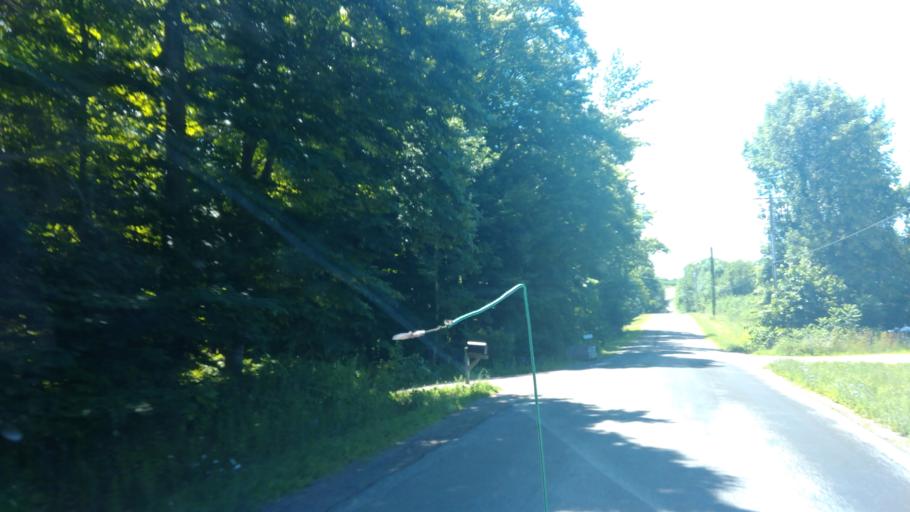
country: US
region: New York
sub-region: Wayne County
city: Lyons
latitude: 43.1480
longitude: -76.9717
